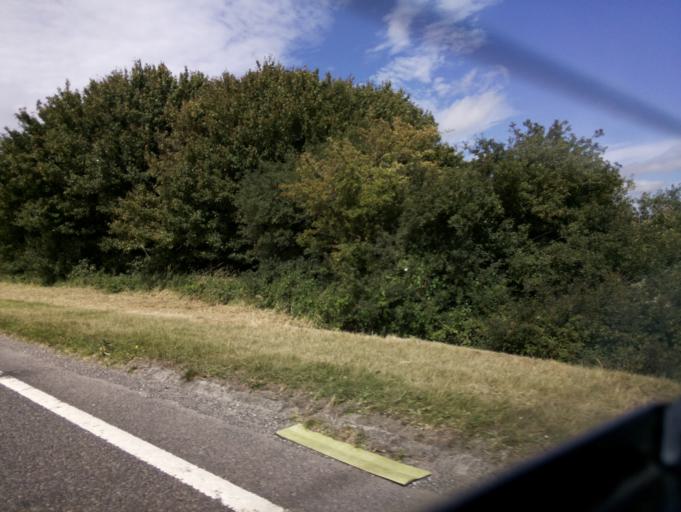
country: GB
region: England
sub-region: Dorset
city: Dorchester
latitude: 50.7980
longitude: -2.5493
